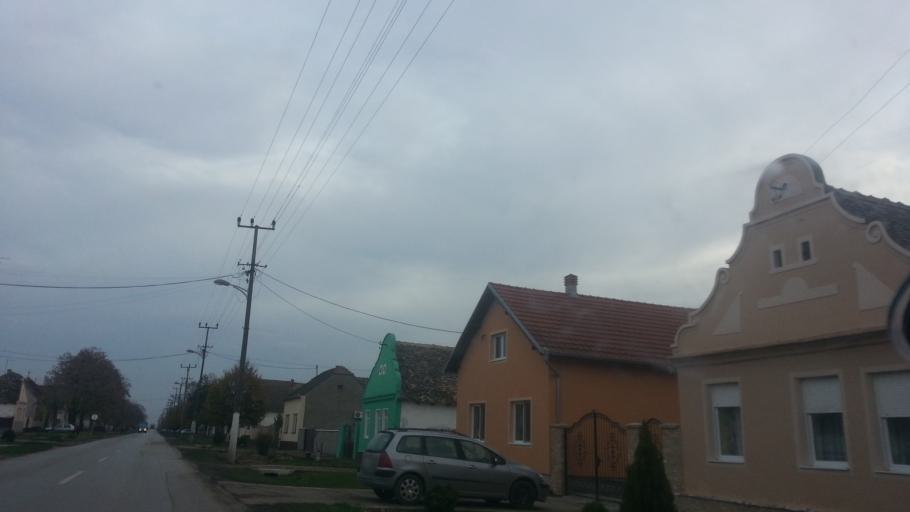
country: RS
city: Golubinci
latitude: 44.9832
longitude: 20.0702
